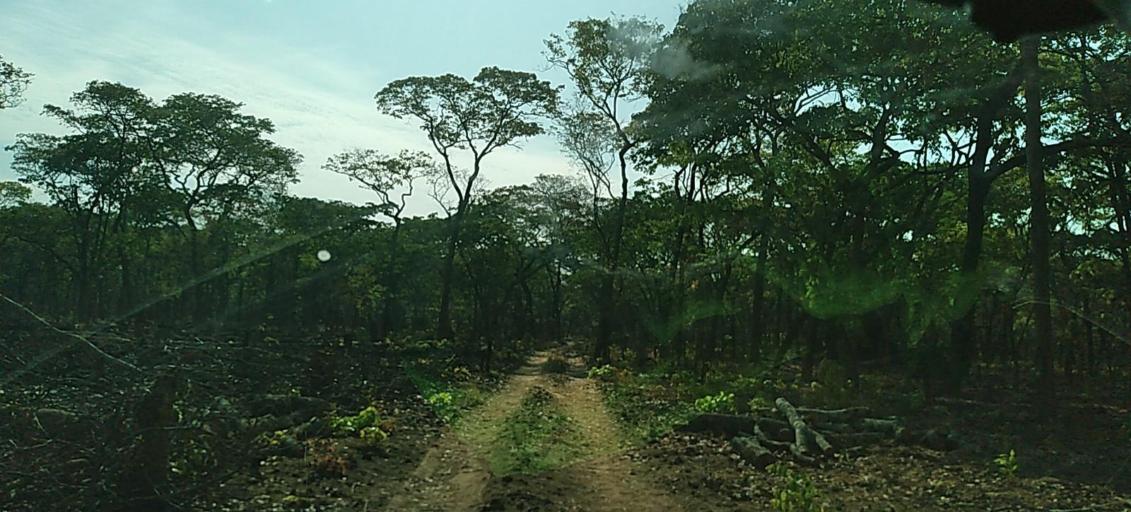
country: ZM
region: North-Western
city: Kalengwa
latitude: -13.2336
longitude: 25.0700
